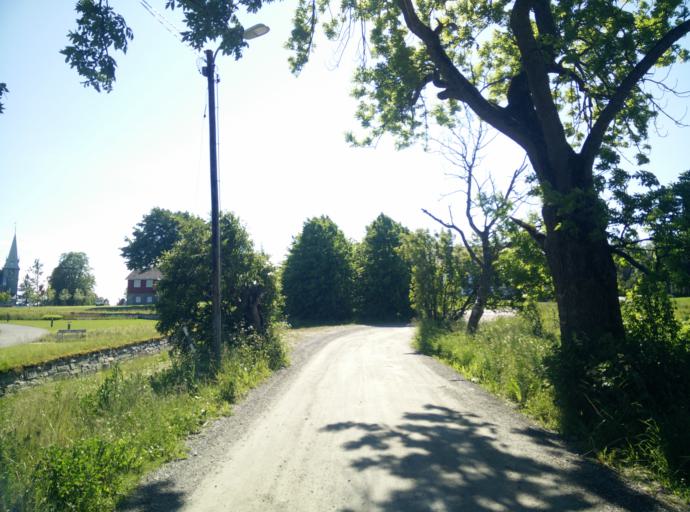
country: NO
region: Sor-Trondelag
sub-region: Trondheim
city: Trondheim
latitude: 63.4068
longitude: 10.3714
